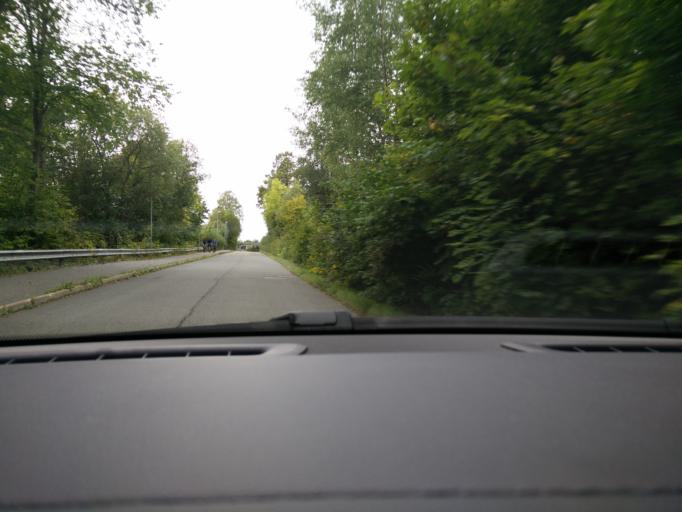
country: NO
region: Akershus
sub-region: Asker
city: Blakstad
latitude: 59.8234
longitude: 10.4583
